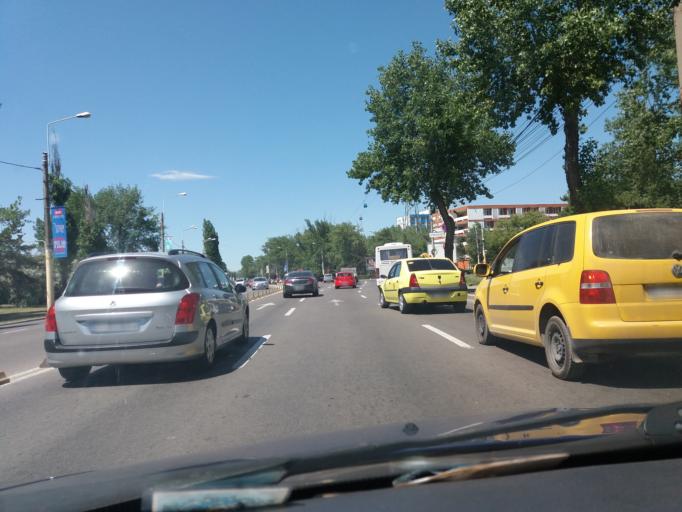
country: RO
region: Constanta
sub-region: Municipiul Constanta
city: Palazu Mare
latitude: 44.2241
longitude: 28.6287
